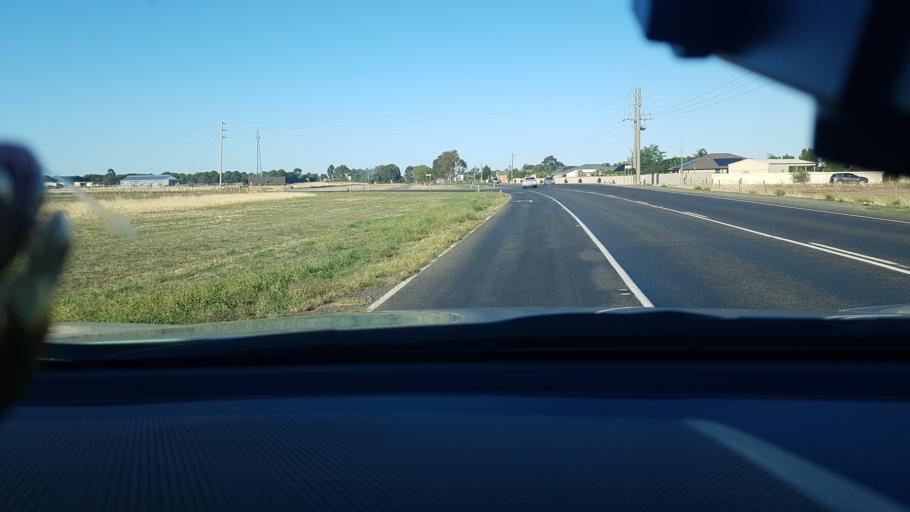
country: AU
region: Victoria
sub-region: Horsham
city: Horsham
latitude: -36.7260
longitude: 142.1677
